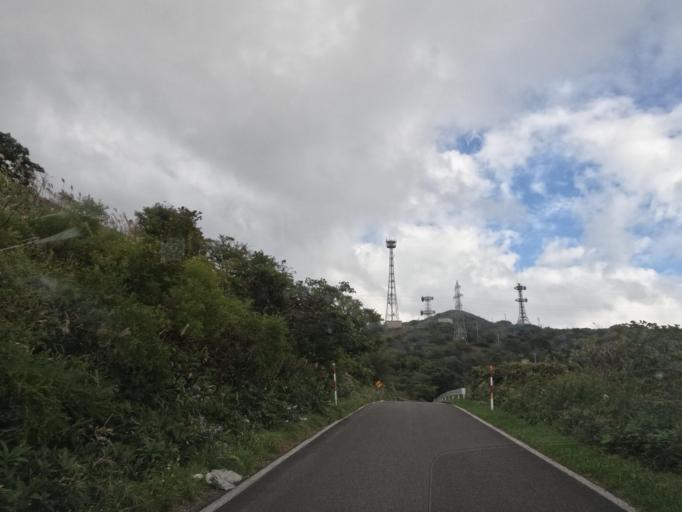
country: JP
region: Hokkaido
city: Muroran
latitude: 42.3222
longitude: 141.0038
